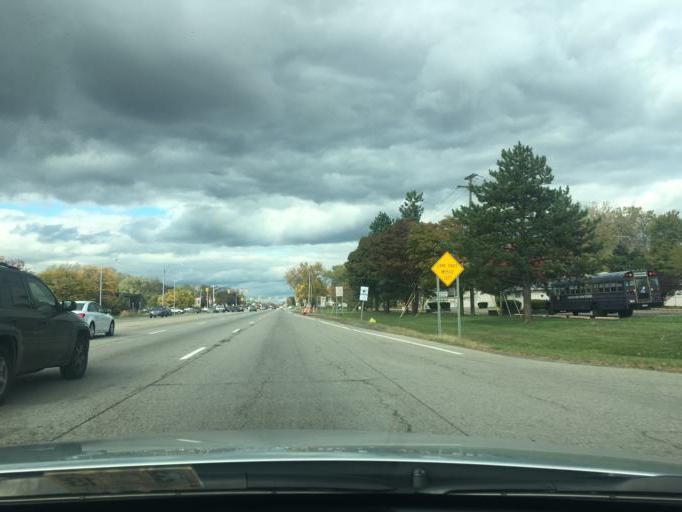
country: US
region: Michigan
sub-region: Oakland County
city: Southfield
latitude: 42.4633
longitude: -83.2205
